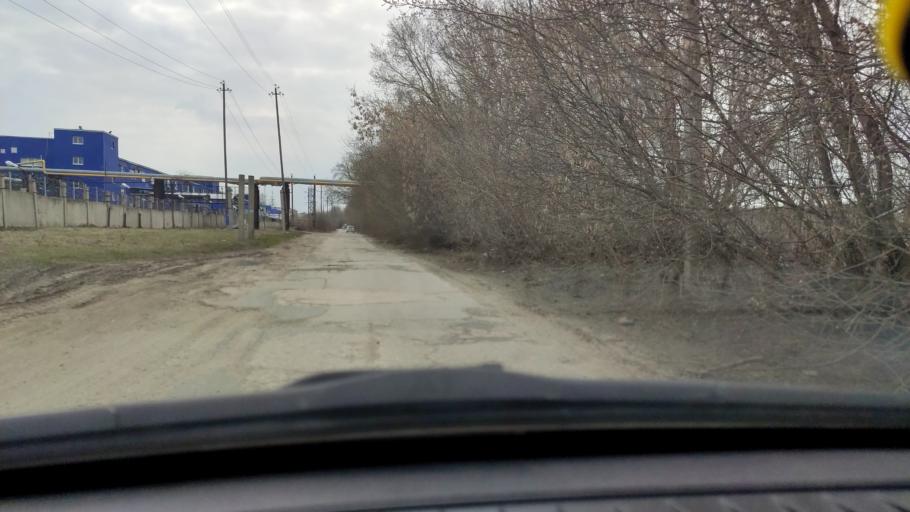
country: RU
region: Samara
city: Tol'yatti
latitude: 53.5245
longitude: 49.4564
